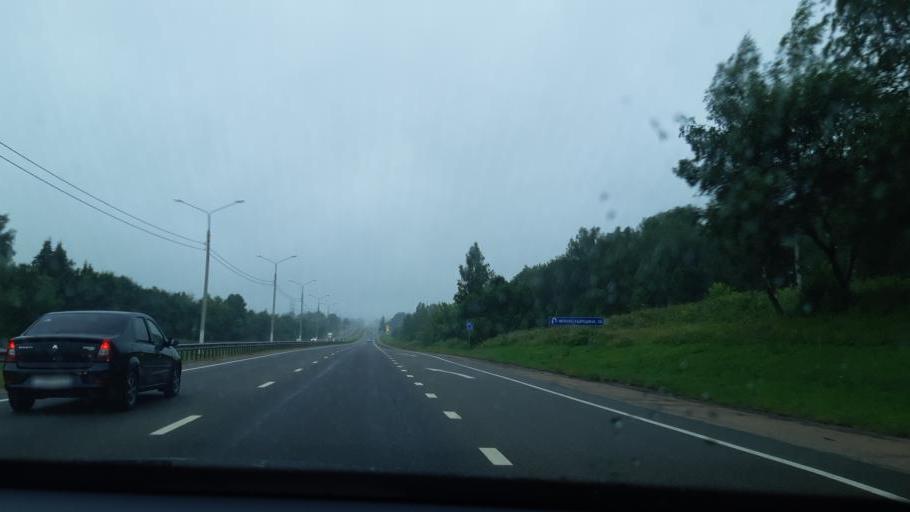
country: RU
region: Smolensk
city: Talashkino
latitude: 54.6513
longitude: 32.1676
